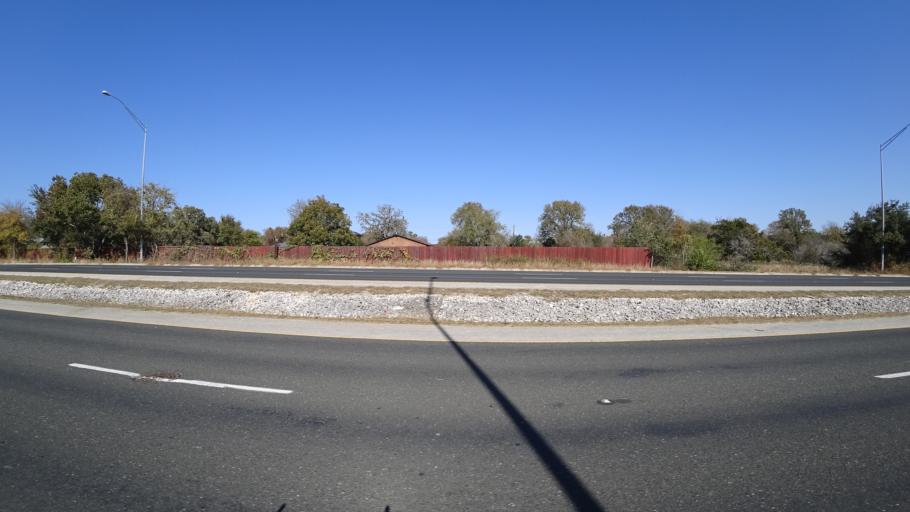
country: US
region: Texas
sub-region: Travis County
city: Barton Creek
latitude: 30.2259
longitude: -97.8570
